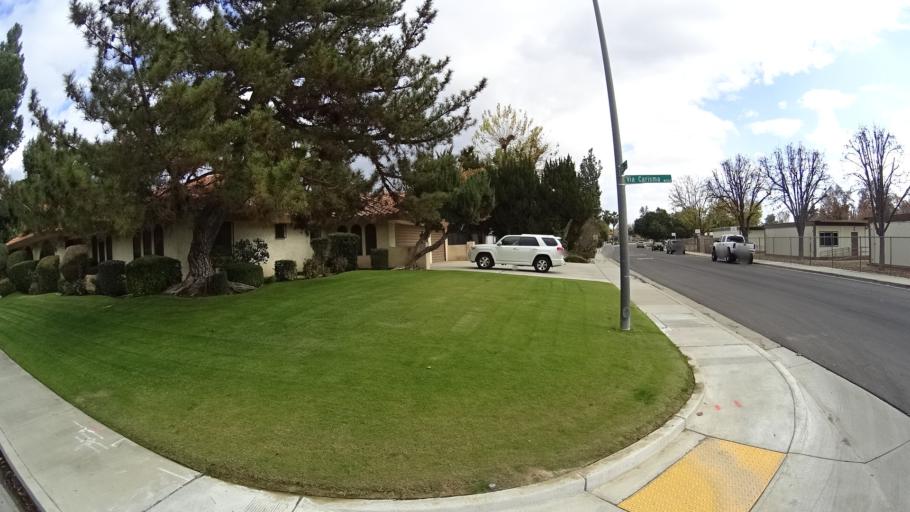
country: US
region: California
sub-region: Kern County
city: Greenacres
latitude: 35.3502
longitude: -119.0886
